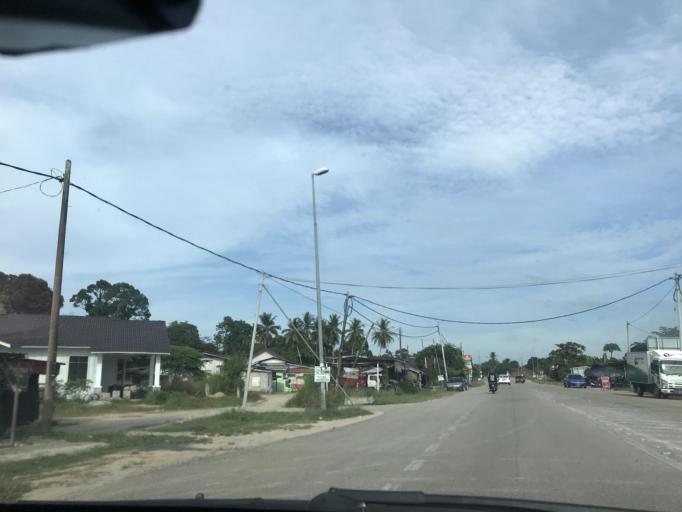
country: MY
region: Kelantan
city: Kota Bharu
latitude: 6.1399
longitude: 102.2030
